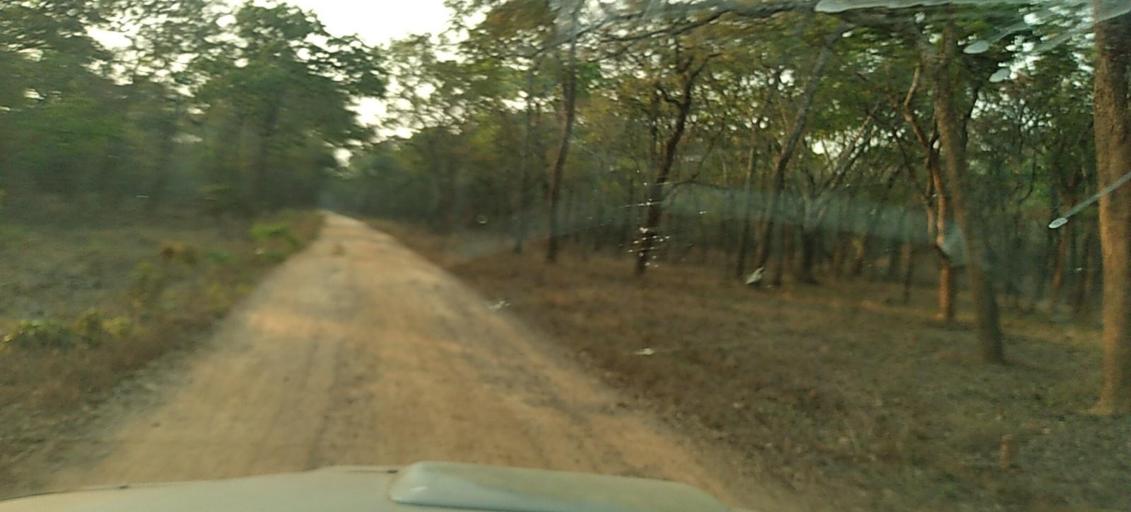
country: ZM
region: North-Western
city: Kasempa
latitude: -13.1620
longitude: 26.4523
